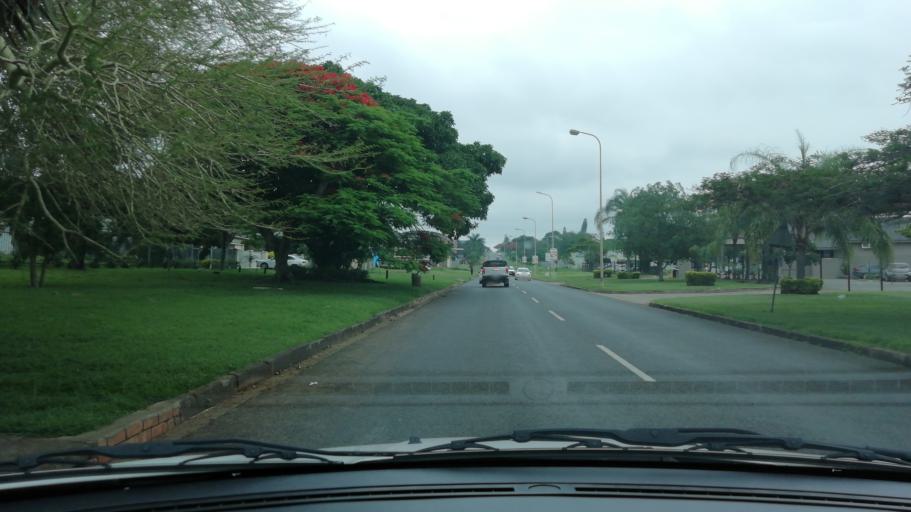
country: ZA
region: KwaZulu-Natal
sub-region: uThungulu District Municipality
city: Empangeni
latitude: -28.7359
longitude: 31.8944
